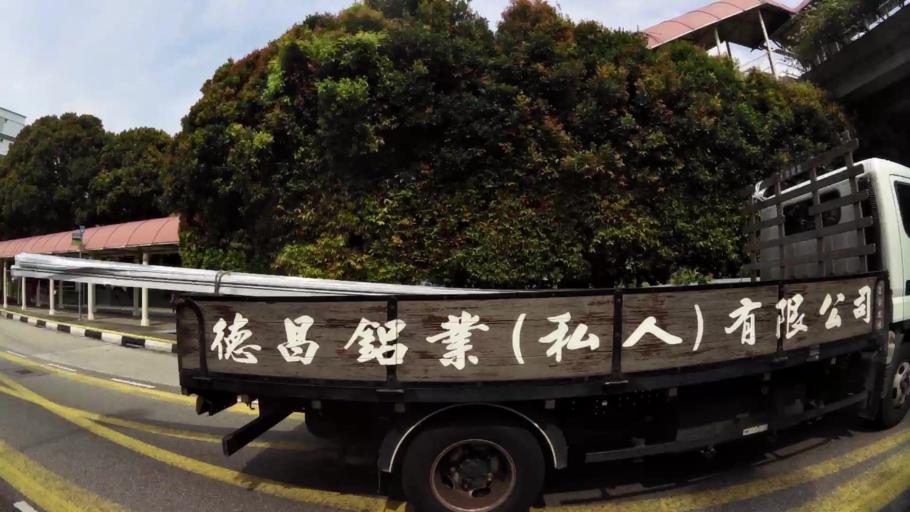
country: SG
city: Singapore
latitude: 1.3649
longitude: 103.9656
